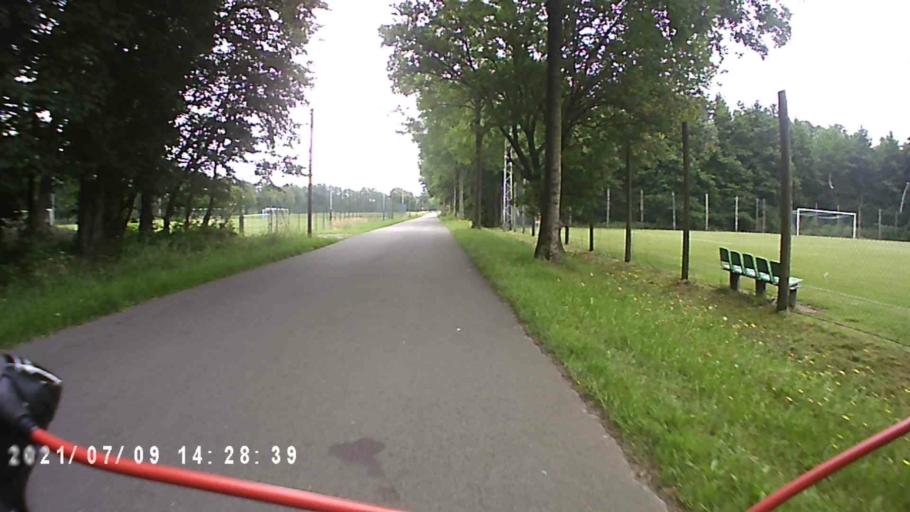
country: DE
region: Lower Saxony
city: Weener
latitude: 53.1286
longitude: 7.2982
